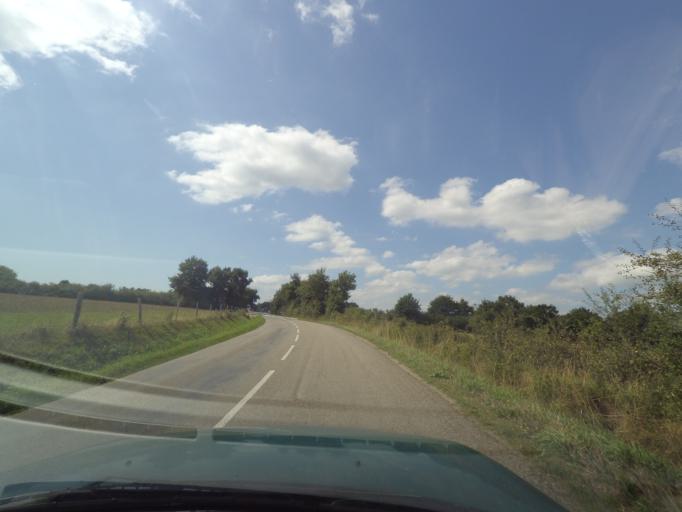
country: FR
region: Pays de la Loire
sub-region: Departement de la Loire-Atlantique
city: Saint-Hilaire-de-Chaleons
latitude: 47.1007
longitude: -1.8557
